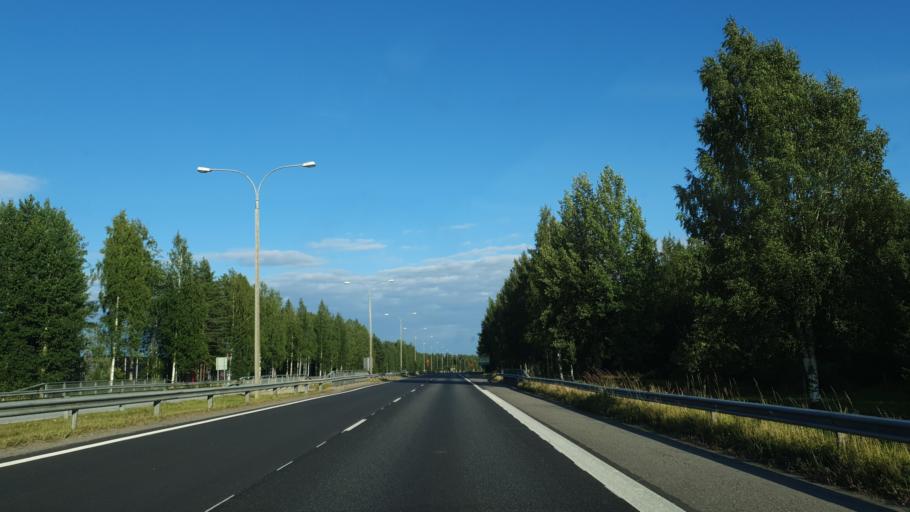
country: FI
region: North Karelia
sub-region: Joensuu
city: Joensuu
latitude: 62.6257
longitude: 29.7079
